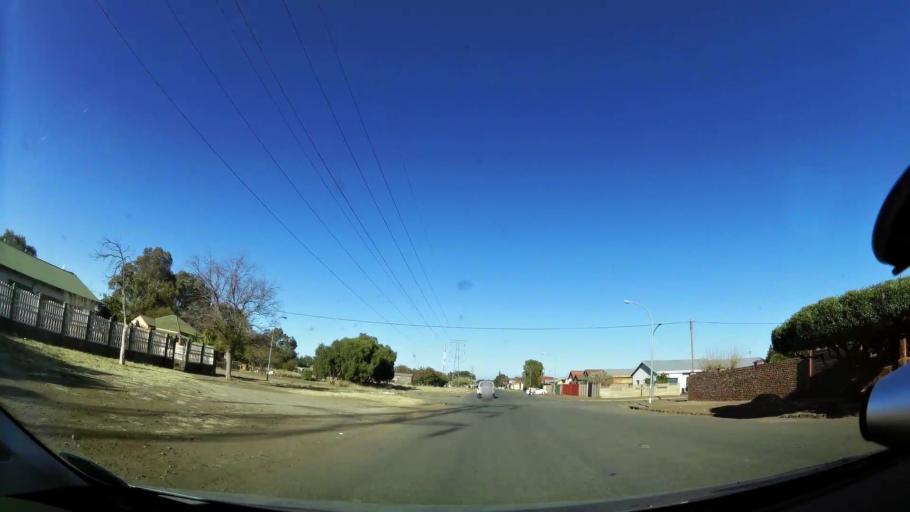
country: ZA
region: Northern Cape
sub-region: Frances Baard District Municipality
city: Kimberley
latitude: -28.7597
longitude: 24.7844
